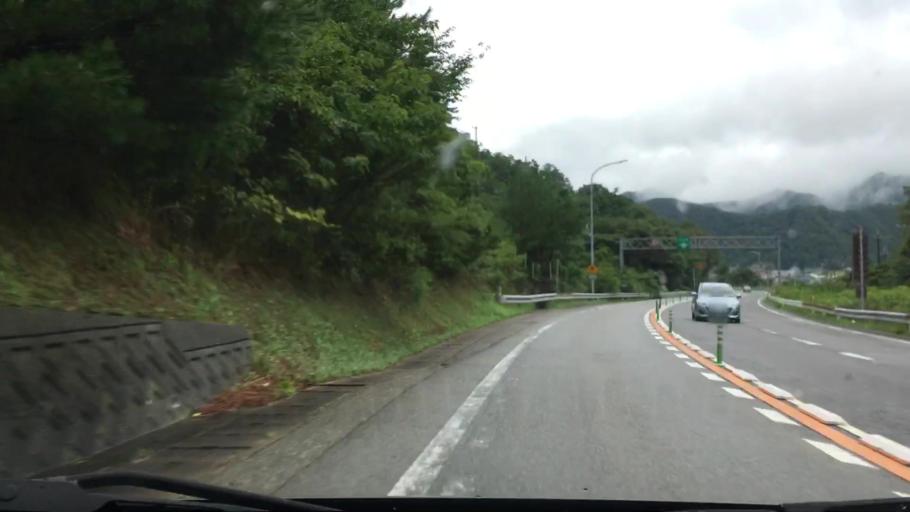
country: JP
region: Hyogo
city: Himeji
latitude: 35.0164
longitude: 134.7649
